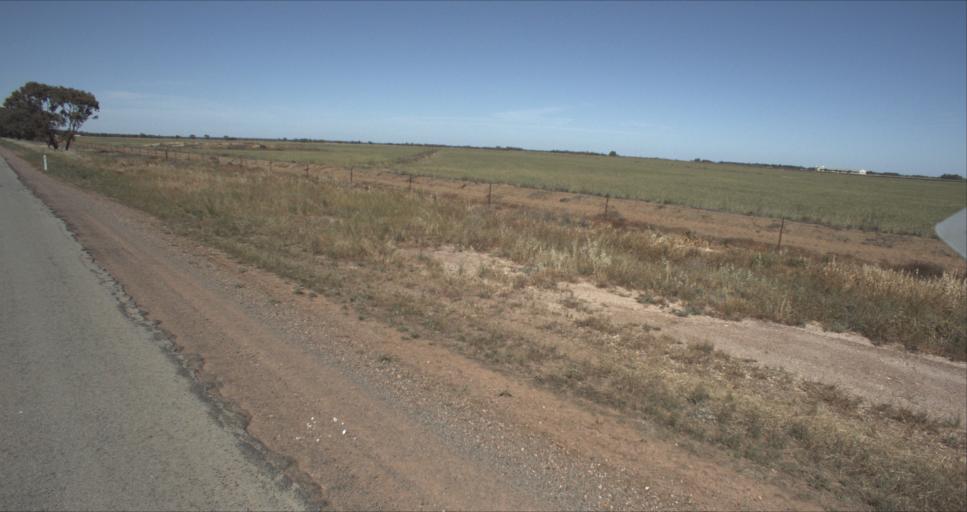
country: AU
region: New South Wales
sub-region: Leeton
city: Leeton
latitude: -34.5537
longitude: 146.3141
